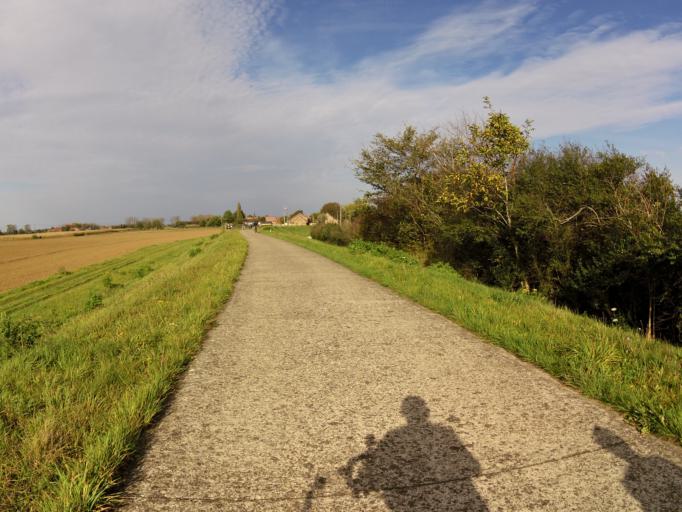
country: BE
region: Flanders
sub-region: Provincie Limburg
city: Maaseik
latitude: 51.0689
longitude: 5.7907
